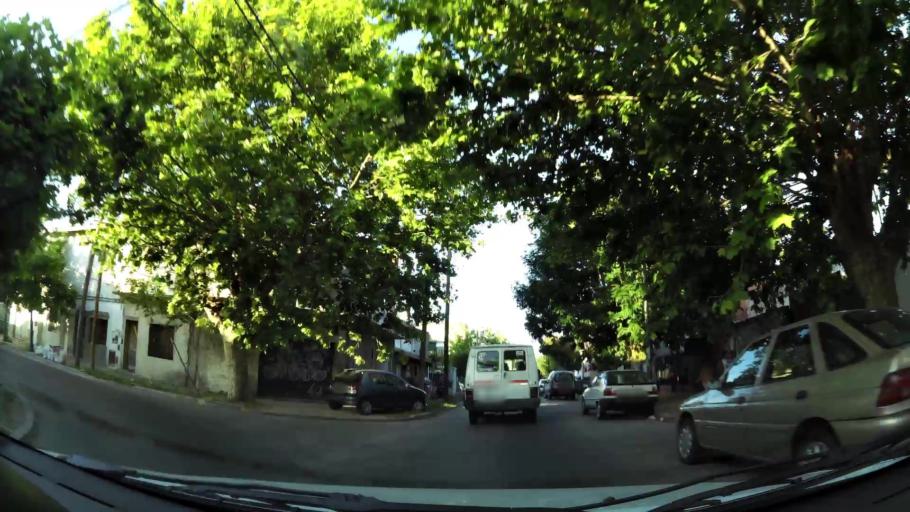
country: AR
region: Buenos Aires
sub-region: Partido de General San Martin
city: General San Martin
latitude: -34.5647
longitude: -58.5302
